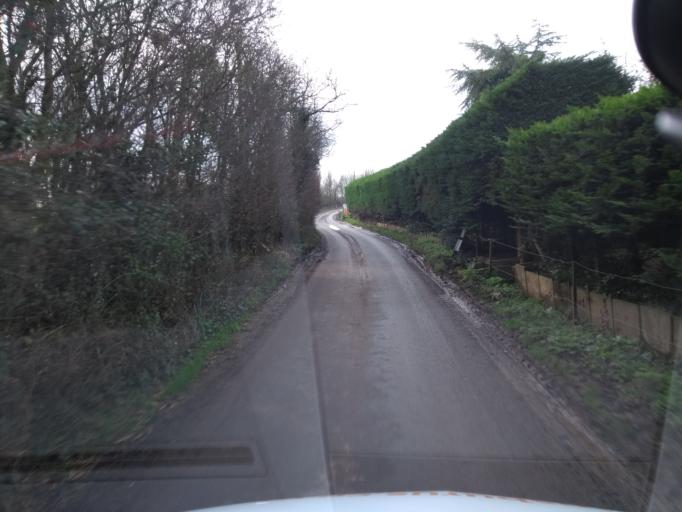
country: GB
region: England
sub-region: Somerset
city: Westonzoyland
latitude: 51.0884
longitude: -2.9076
